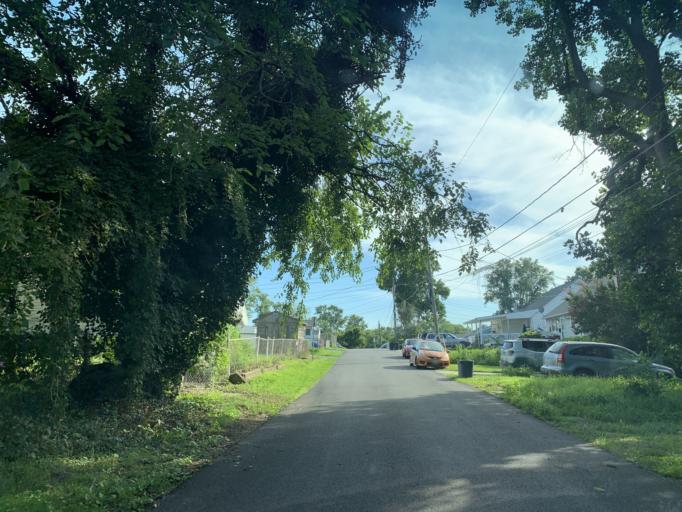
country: US
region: Maryland
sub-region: Baltimore County
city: Essex
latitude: 39.3073
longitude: -76.4878
